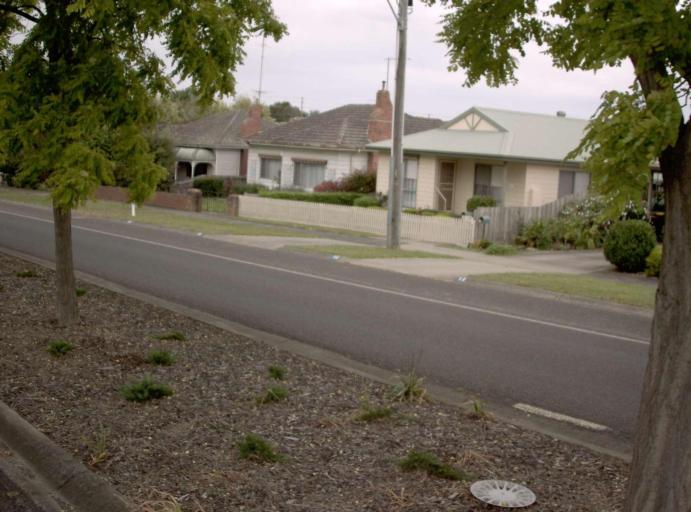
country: AU
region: Victoria
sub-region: Baw Baw
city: Warragul
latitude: -38.4829
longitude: 145.9501
